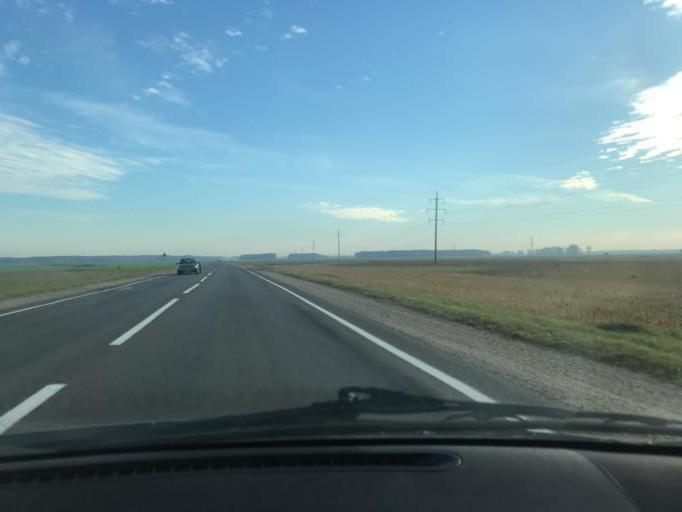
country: BY
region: Brest
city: Drahichyn
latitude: 52.2014
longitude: 25.0481
